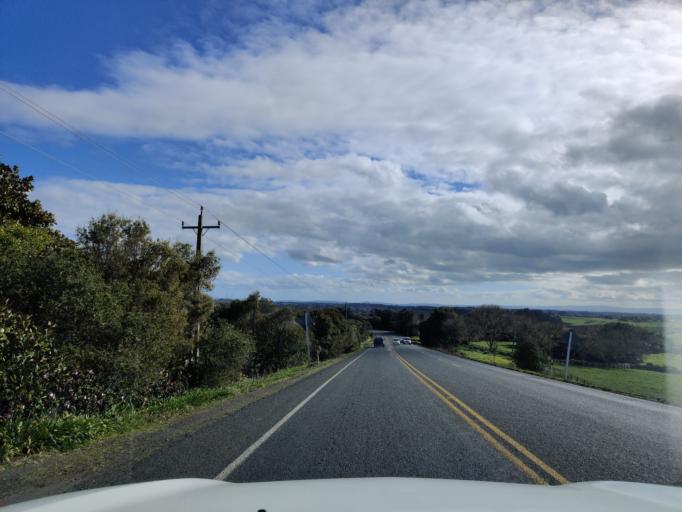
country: NZ
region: Auckland
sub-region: Auckland
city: Pukekohe East
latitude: -37.1961
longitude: 174.9388
